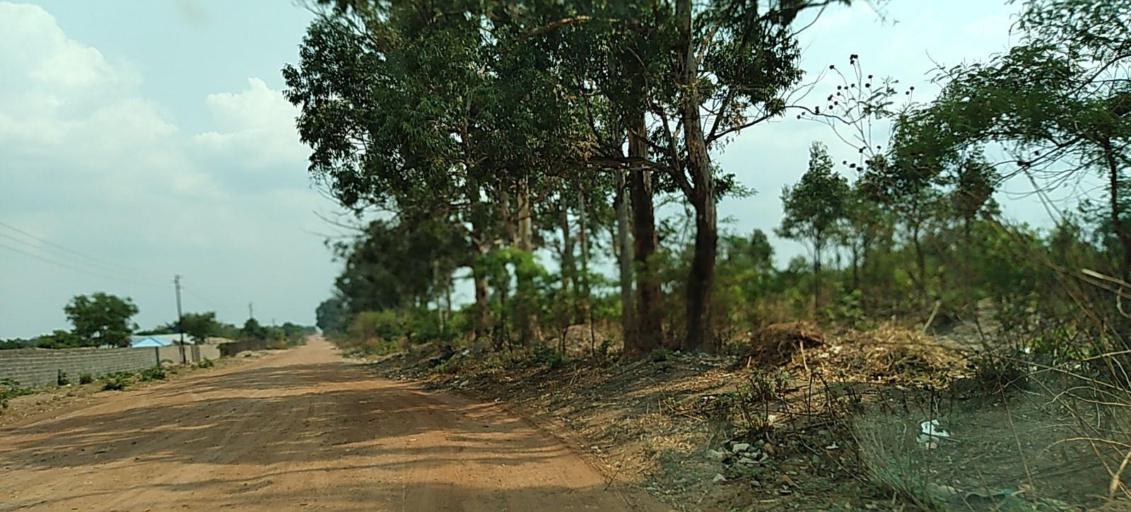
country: ZM
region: Copperbelt
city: Kalulushi
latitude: -12.8329
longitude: 28.0773
